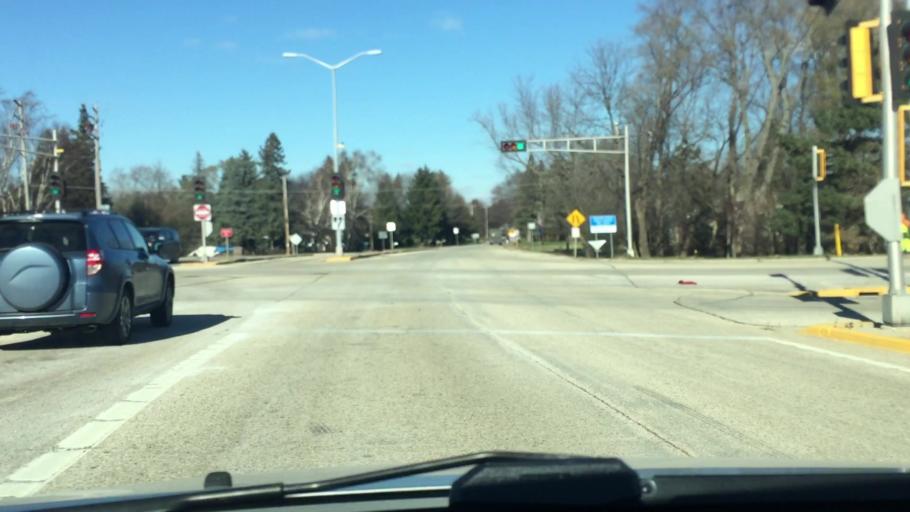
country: US
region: Wisconsin
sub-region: Waukesha County
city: Pewaukee
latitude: 43.0522
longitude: -88.3041
